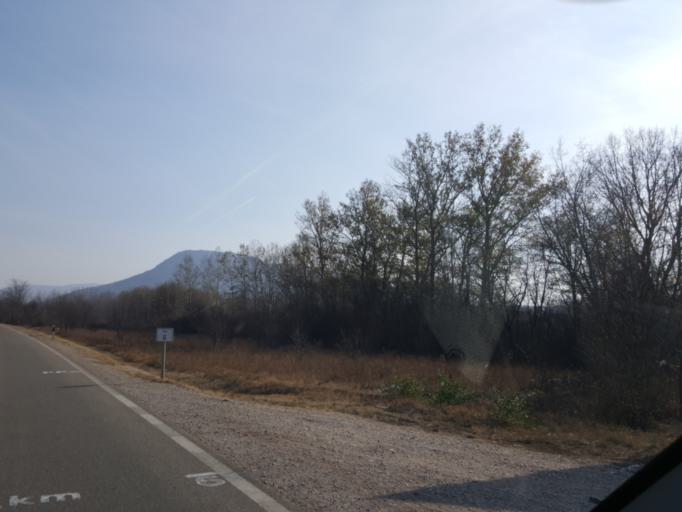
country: RS
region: Central Serbia
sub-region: Pomoravski Okrug
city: Paracin
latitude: 43.8642
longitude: 21.5017
